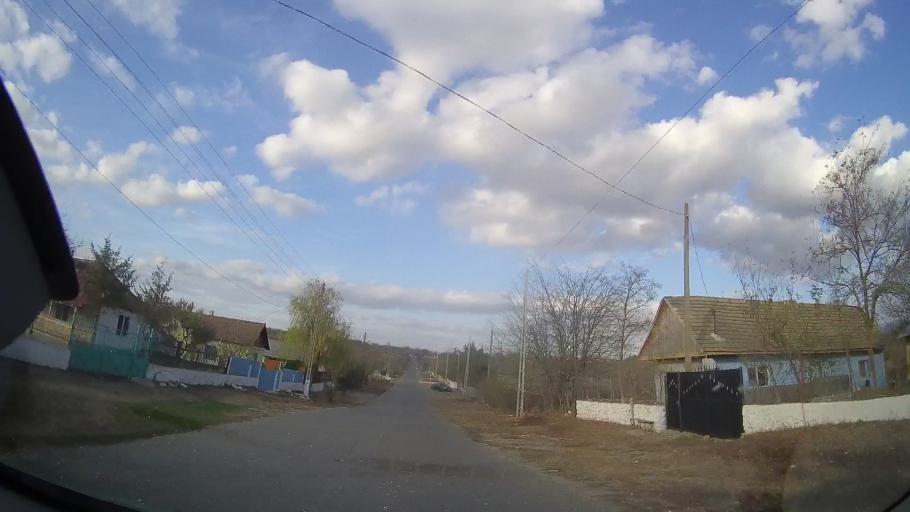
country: RO
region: Constanta
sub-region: Comuna Cerchezu
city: Cerchezu
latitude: 43.8554
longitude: 28.1012
